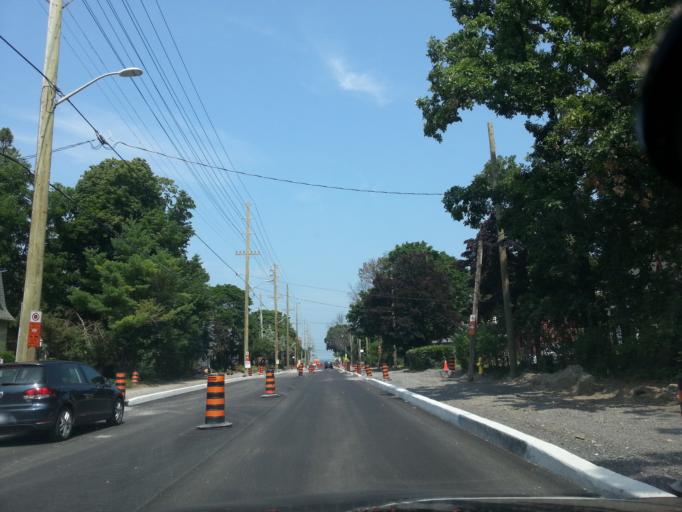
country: CA
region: Ontario
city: Ottawa
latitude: 45.3878
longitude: -75.7511
